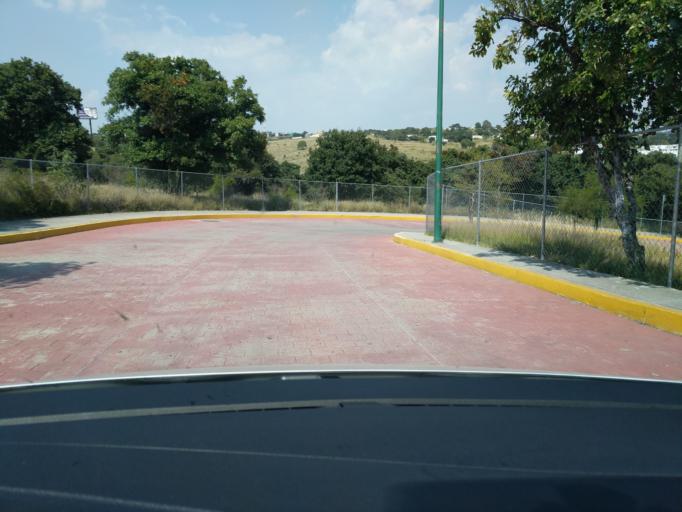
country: MX
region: Puebla
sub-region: Puebla
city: Galaxia la Calera
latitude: 19.0065
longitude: -98.1475
